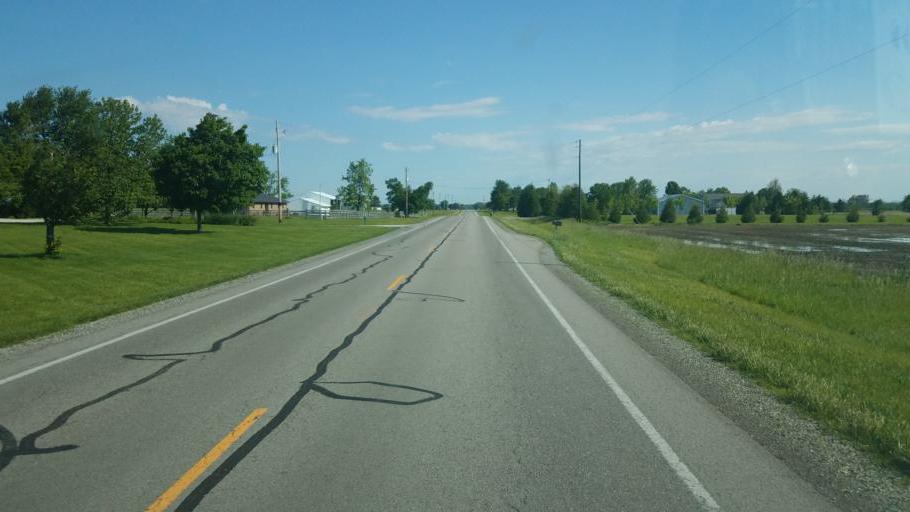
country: US
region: Ohio
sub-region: Hardin County
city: Kenton
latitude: 40.6042
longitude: -83.5947
